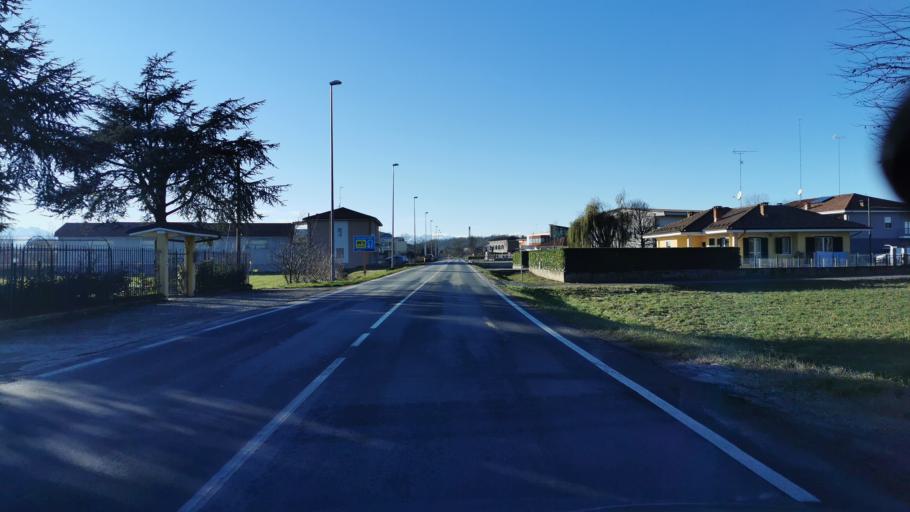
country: IT
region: Piedmont
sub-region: Provincia di Cuneo
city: Carru
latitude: 44.4741
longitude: 7.8590
